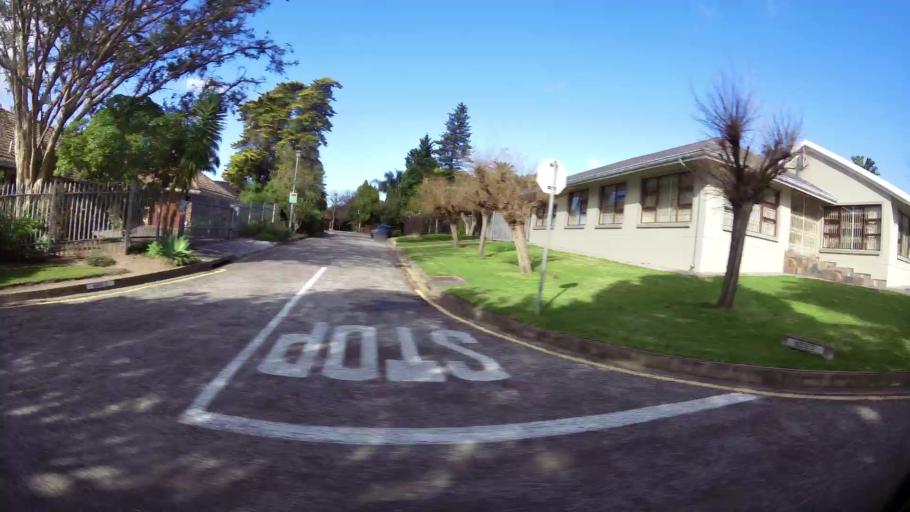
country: ZA
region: Western Cape
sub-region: Eden District Municipality
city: George
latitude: -33.9576
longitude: 22.4879
